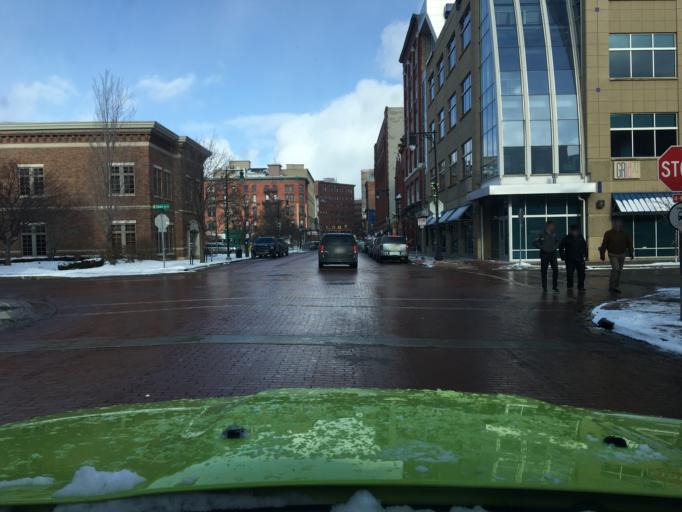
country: US
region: Michigan
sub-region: Kent County
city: Grand Rapids
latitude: 42.9608
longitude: -85.6702
